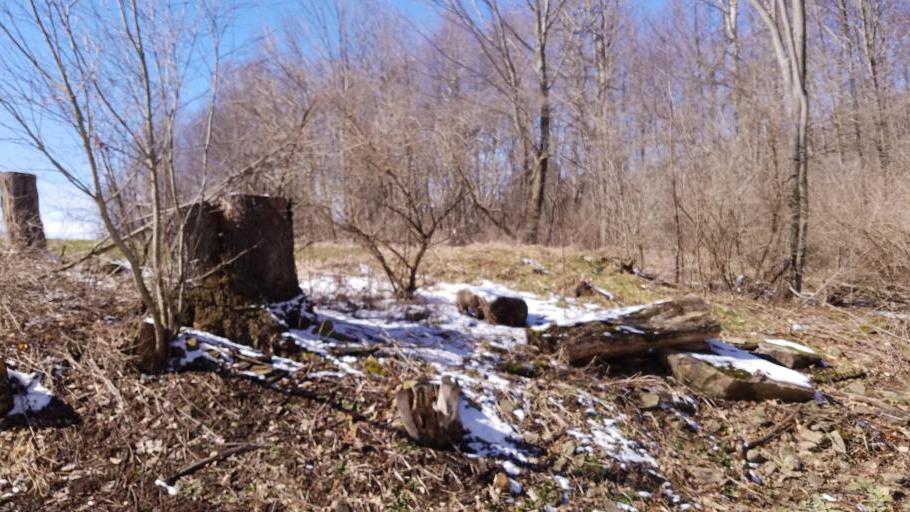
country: US
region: New York
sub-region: Allegany County
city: Wellsville
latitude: 42.0055
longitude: -77.9296
